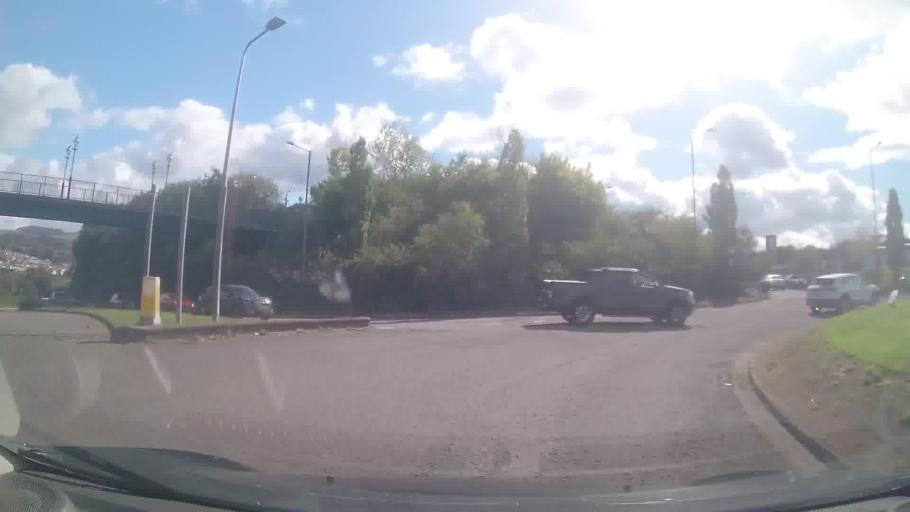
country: GB
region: Wales
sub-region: Merthyr Tydfil County Borough
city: Merthyr Tydfil
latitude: 51.7491
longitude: -3.3935
